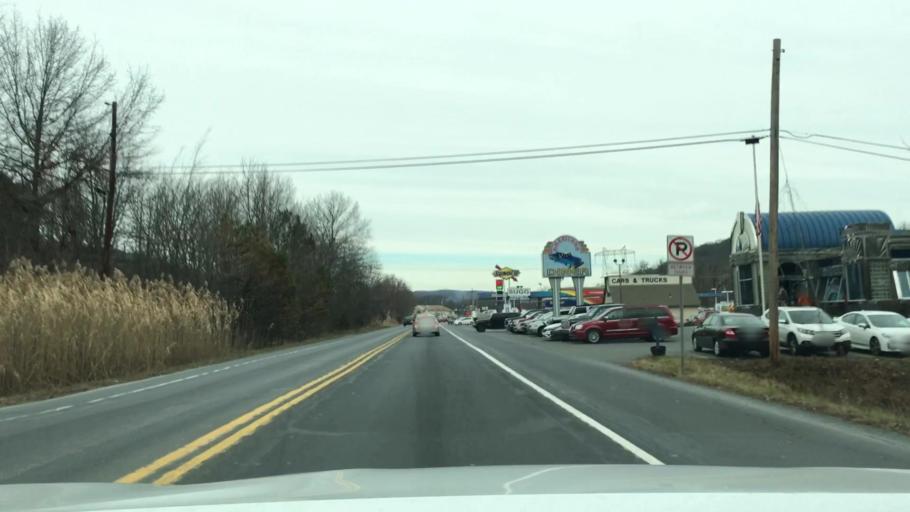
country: US
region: Pennsylvania
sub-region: Berks County
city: New Berlinville
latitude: 40.3554
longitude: -75.6280
